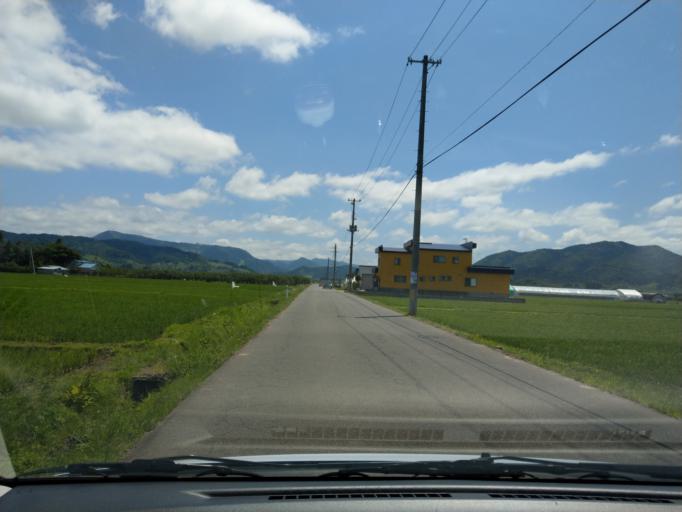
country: JP
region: Aomori
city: Hirosaki
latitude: 40.5641
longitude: 140.5514
